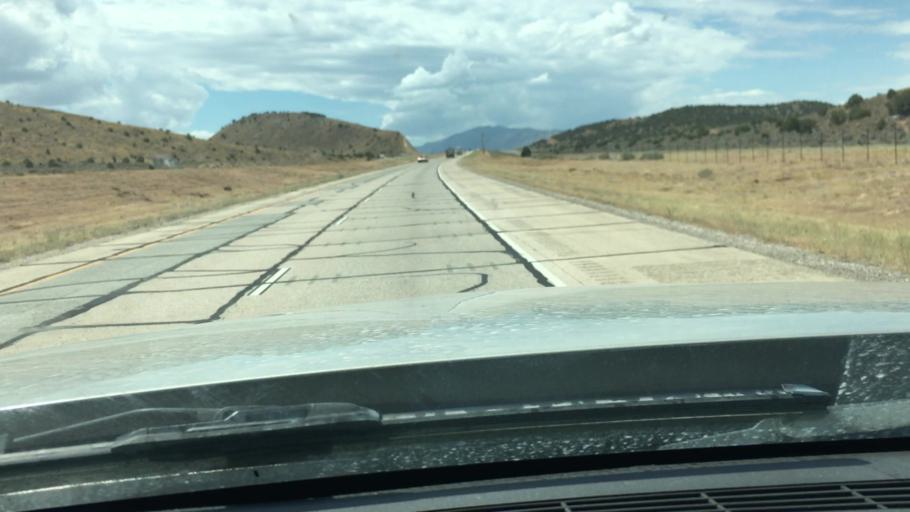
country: US
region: Utah
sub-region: Sanpete County
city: Gunnison
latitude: 39.3386
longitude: -112.0811
